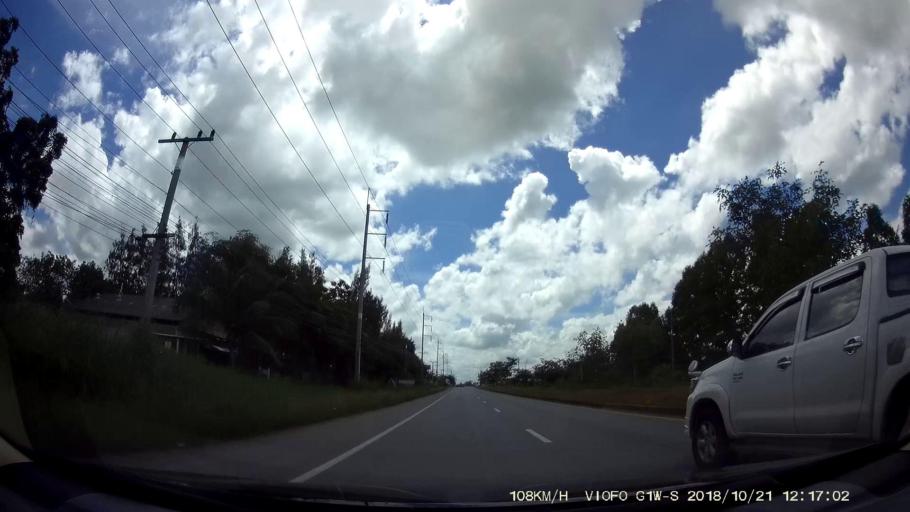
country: TH
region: Nakhon Ratchasima
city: Dan Khun Thot
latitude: 15.3381
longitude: 101.8227
